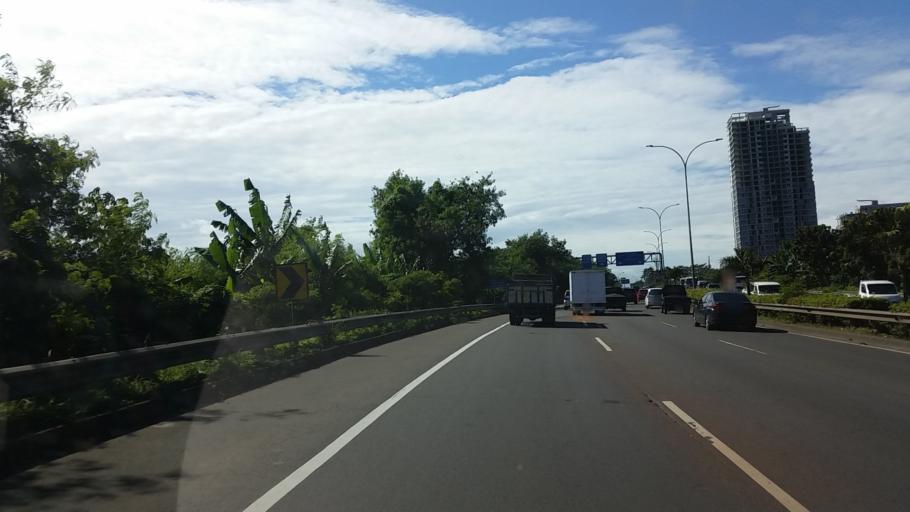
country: ID
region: Banten
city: South Tangerang
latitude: -6.2696
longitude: 106.7685
